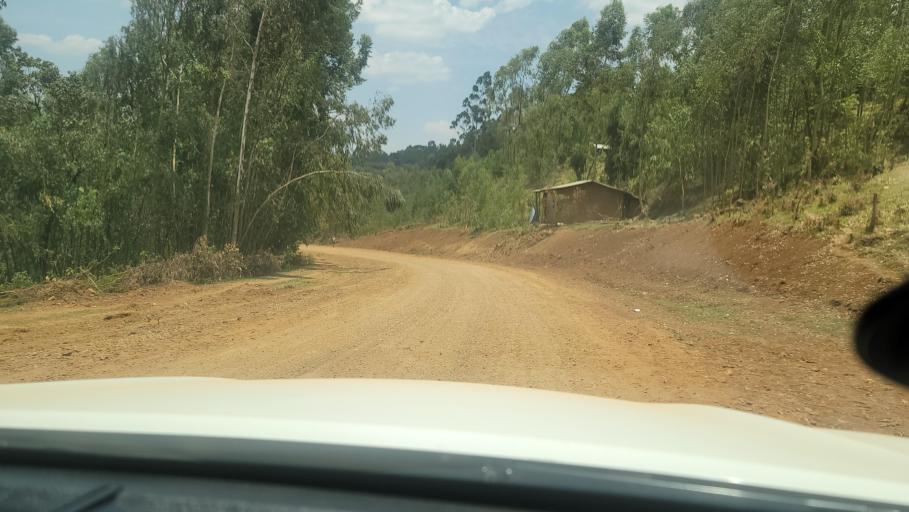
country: ET
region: Oromiya
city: Agaro
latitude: 7.8010
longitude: 36.4660
